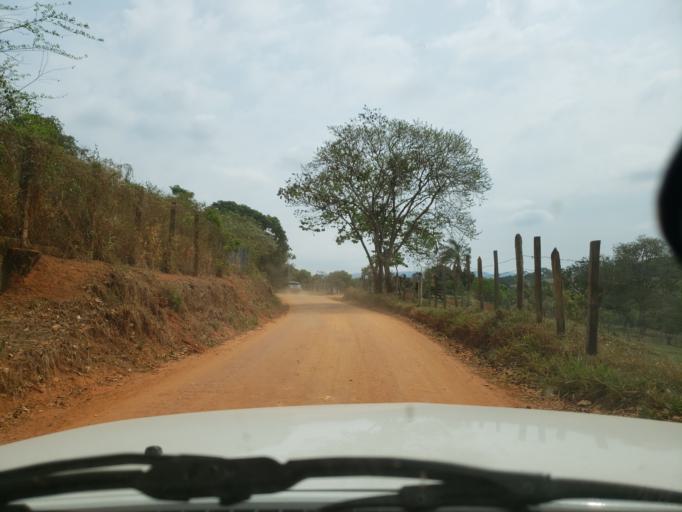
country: BR
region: Minas Gerais
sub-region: Jacutinga
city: Jacutinga
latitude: -22.3109
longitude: -46.6047
